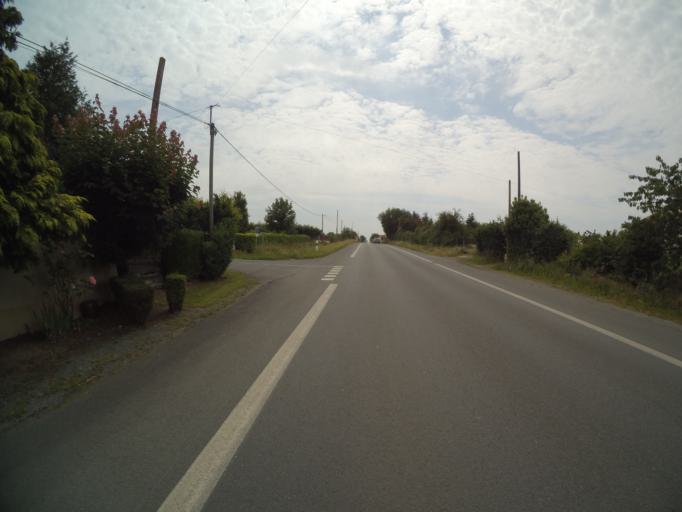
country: FR
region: Pays de la Loire
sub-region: Departement de la Vendee
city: Chavagnes-en-Paillers
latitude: 46.8916
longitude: -1.2224
